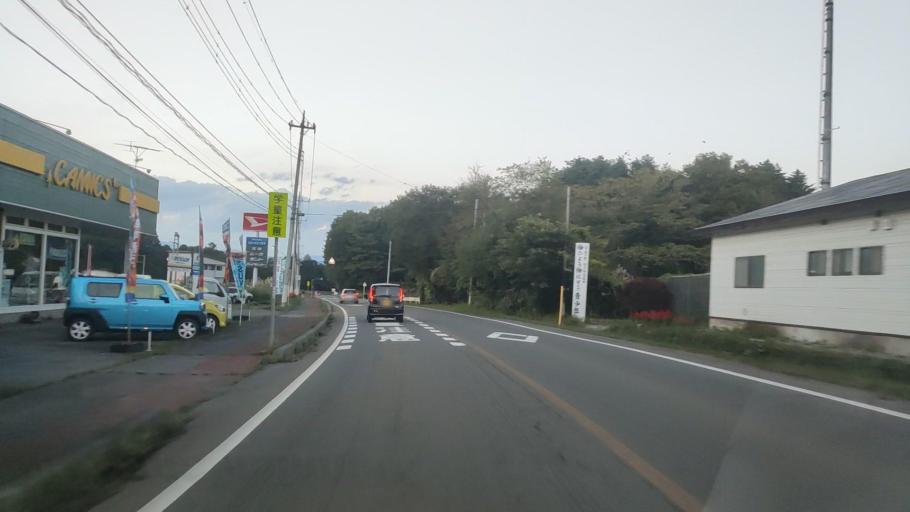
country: JP
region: Nagano
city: Komoro
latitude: 36.5085
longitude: 138.5938
